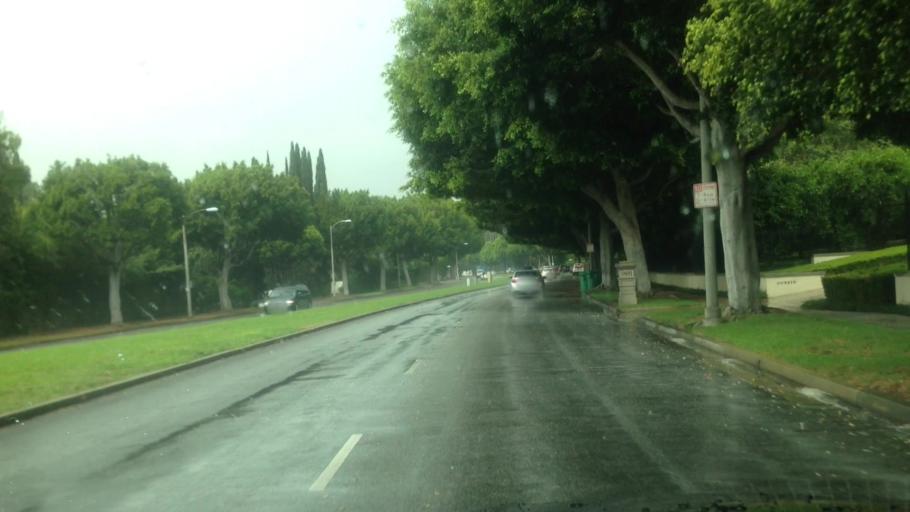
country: US
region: California
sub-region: Los Angeles County
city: Beverly Hills
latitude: 34.0866
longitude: -118.4025
